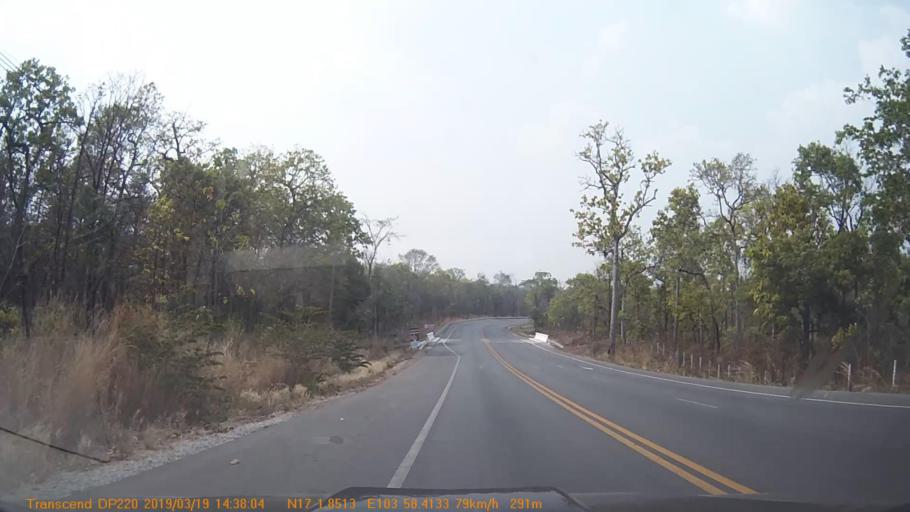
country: TH
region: Sakon Nakhon
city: Phu Phan
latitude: 17.0311
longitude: 103.9733
